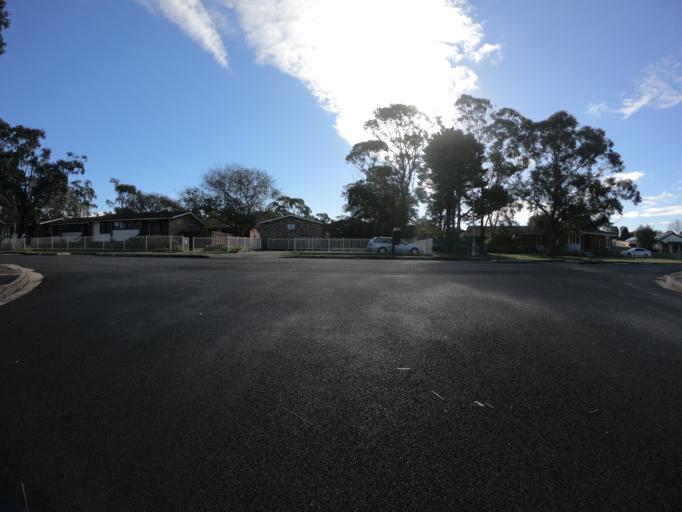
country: AU
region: New South Wales
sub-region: Wollongong
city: East Corrimal
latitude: -34.3696
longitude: 150.9195
